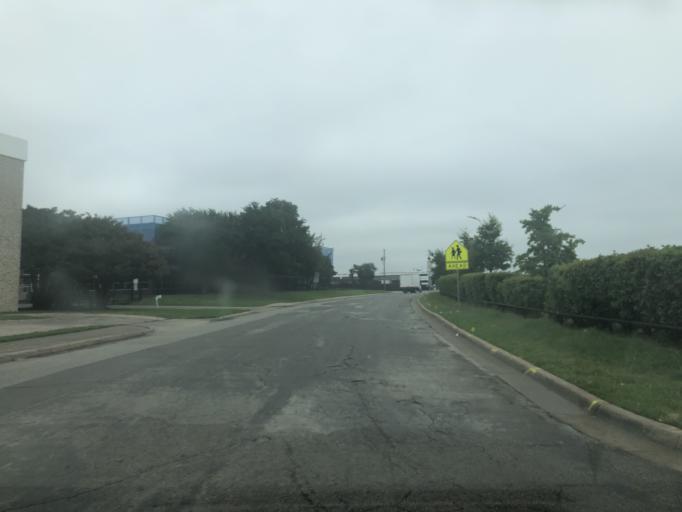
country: US
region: Texas
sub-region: Dallas County
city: University Park
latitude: 32.8589
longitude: -96.8638
